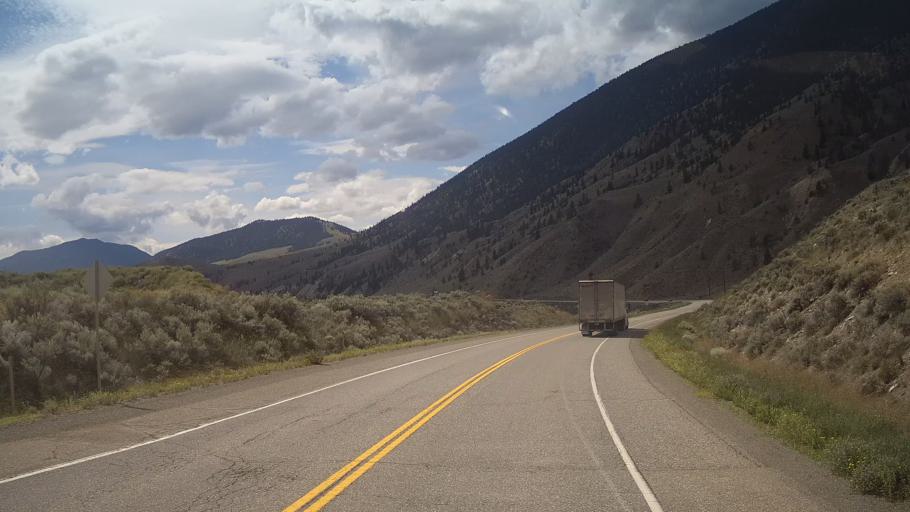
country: CA
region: British Columbia
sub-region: Thompson-Nicola Regional District
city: Ashcroft
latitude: 50.4974
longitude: -121.2885
